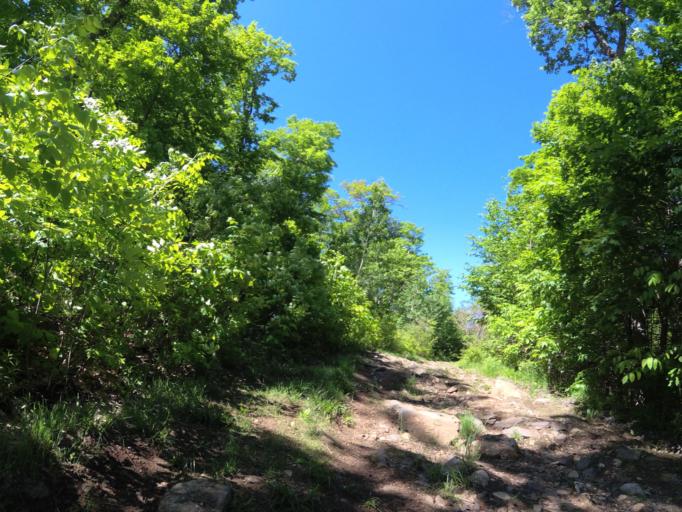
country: CA
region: Ontario
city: Renfrew
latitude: 45.0654
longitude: -77.0753
